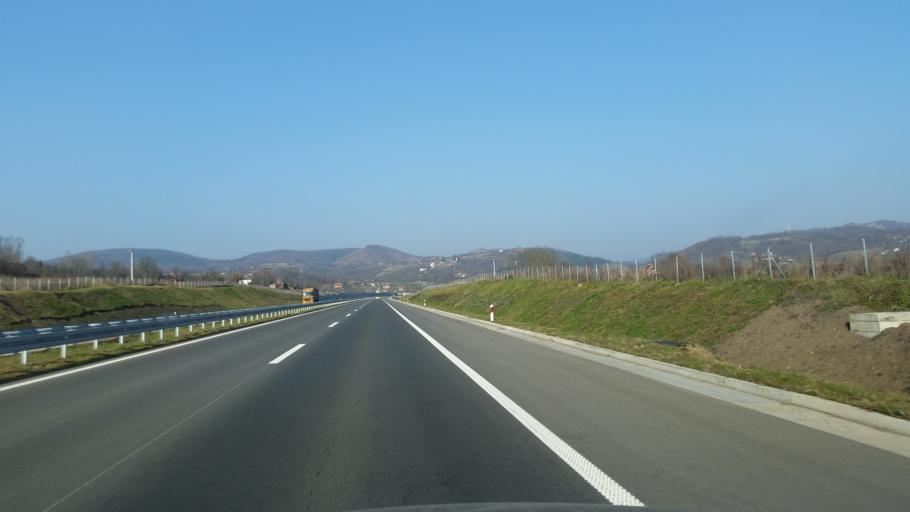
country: RS
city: Prislonica
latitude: 43.9569
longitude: 20.3988
